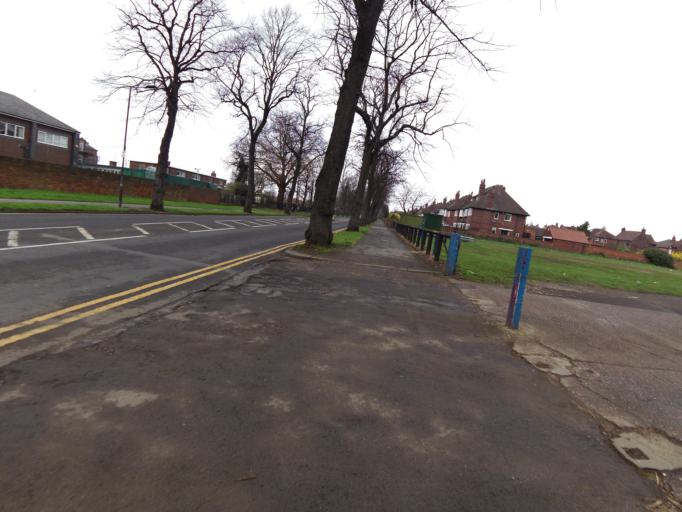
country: GB
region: England
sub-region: Doncaster
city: Doncaster
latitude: 53.5213
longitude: -1.1073
